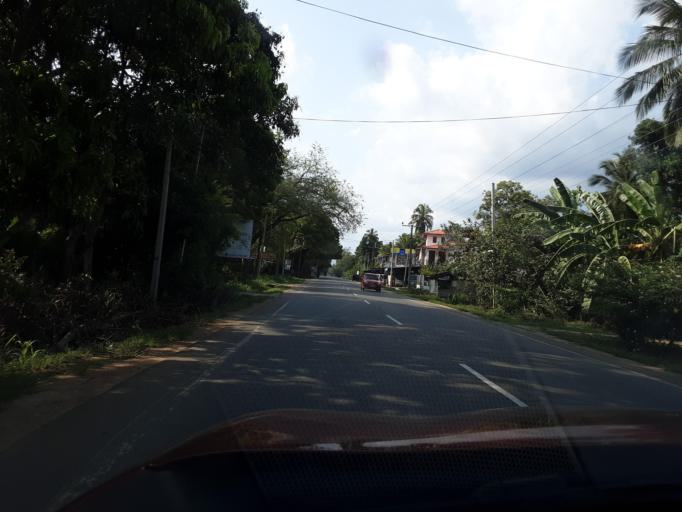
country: LK
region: Uva
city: Haputale
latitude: 6.6612
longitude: 81.1144
